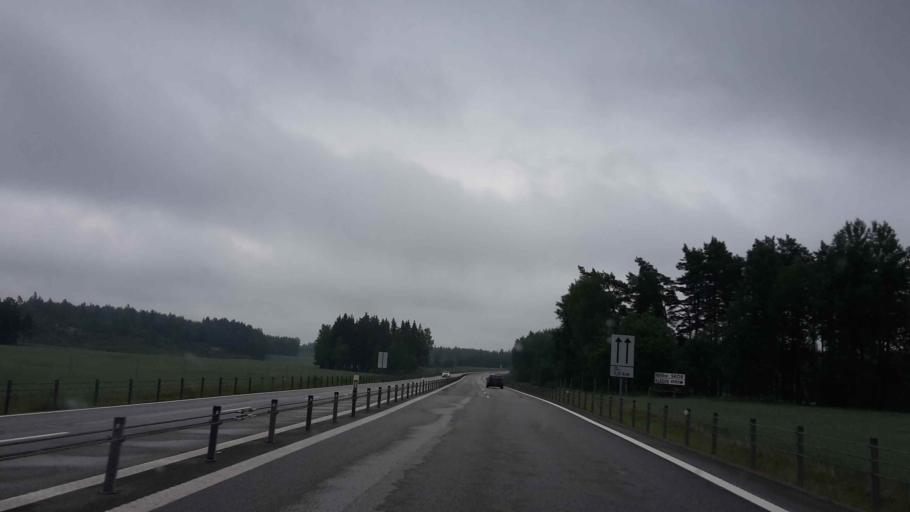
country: SE
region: OEstergoetland
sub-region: Valdemarsviks Kommun
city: Gusum
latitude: 58.3063
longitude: 16.4867
